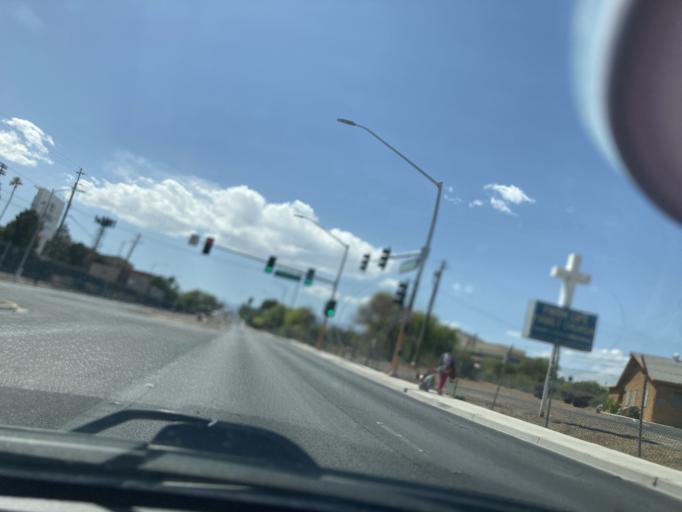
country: US
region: Nevada
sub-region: Clark County
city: Las Vegas
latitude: 36.1813
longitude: -115.1278
